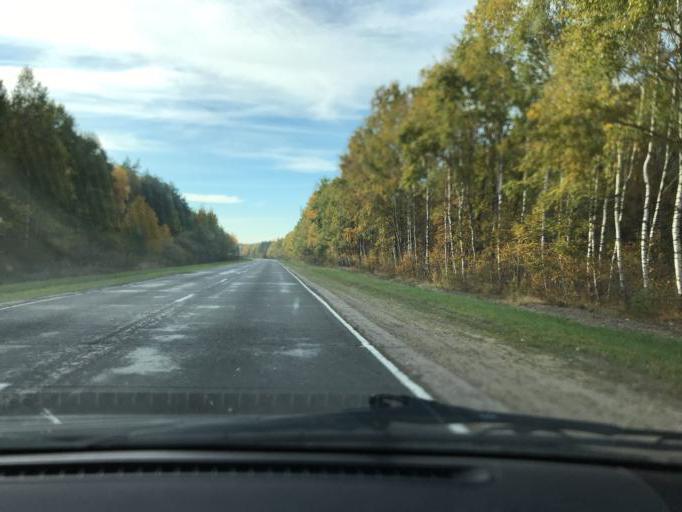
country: BY
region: Brest
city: Ivanava
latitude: 52.1568
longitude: 25.7669
